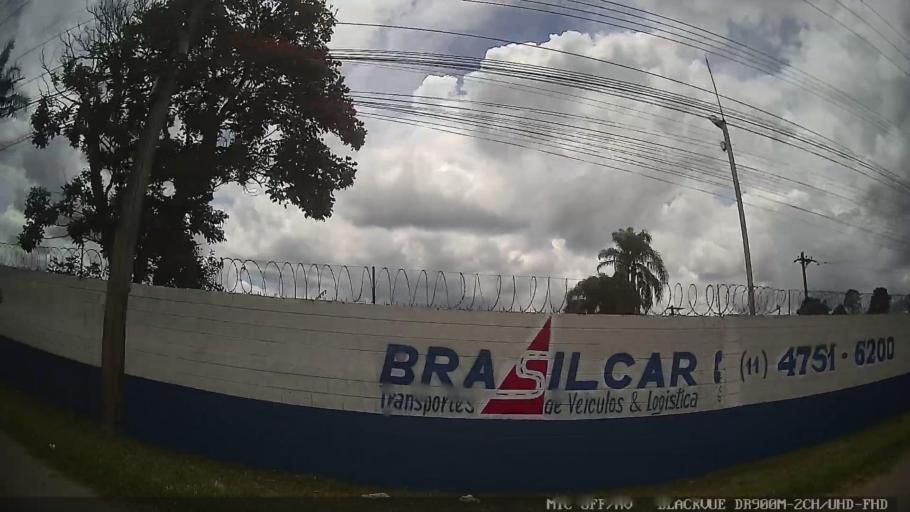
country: BR
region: Sao Paulo
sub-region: Ribeirao Pires
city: Ribeirao Pires
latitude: -23.6582
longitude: -46.3333
